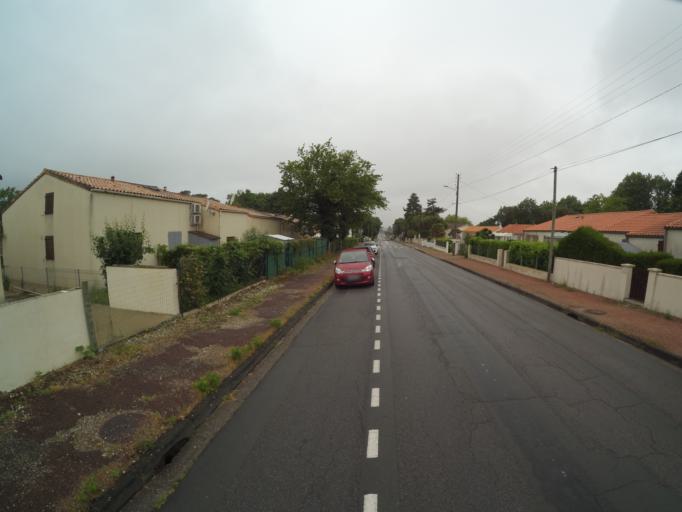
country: FR
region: Poitou-Charentes
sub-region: Departement de la Charente-Maritime
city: Saint-Georges-de-Didonne
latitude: 45.6109
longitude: -0.9968
